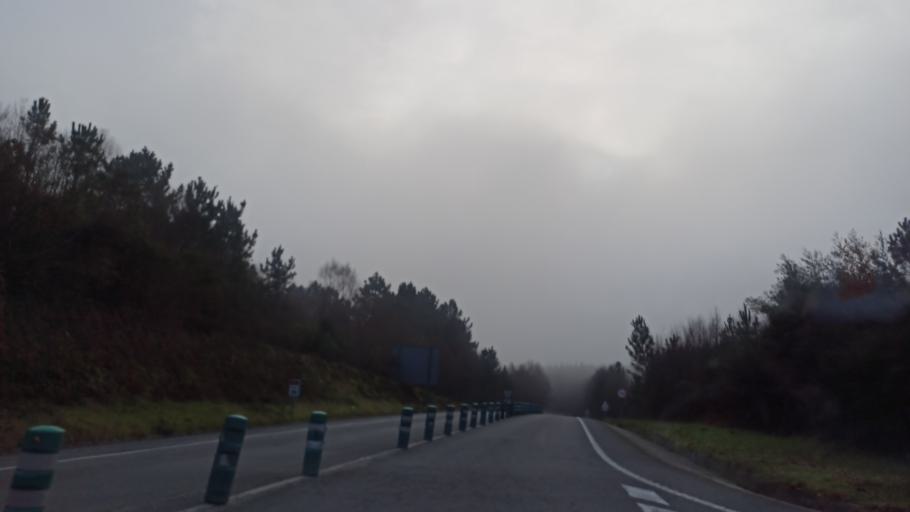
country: ES
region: Galicia
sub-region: Provincia da Coruna
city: As Pontes de Garcia Rodriguez
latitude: 43.4407
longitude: -7.8823
